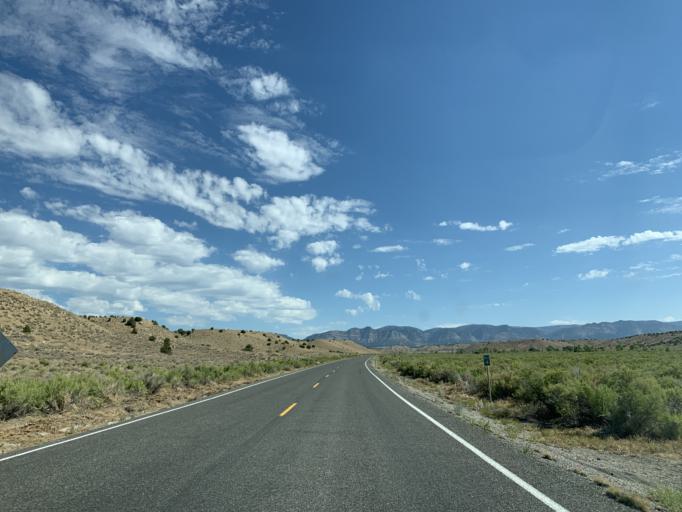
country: US
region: Utah
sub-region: Carbon County
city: Wellington
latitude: 39.5844
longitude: -110.6482
